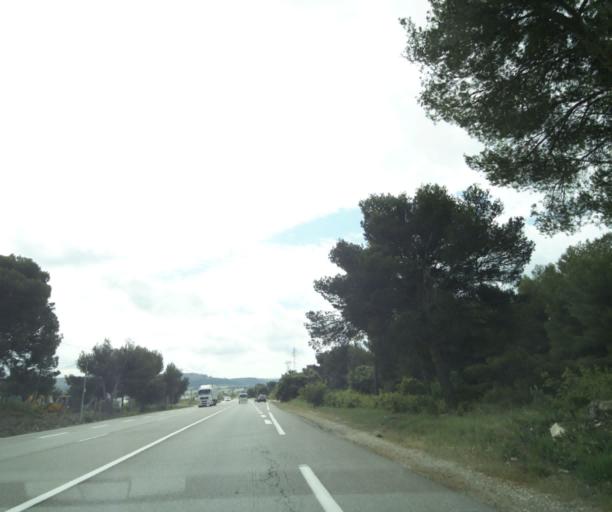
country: FR
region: Provence-Alpes-Cote d'Azur
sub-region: Departement des Bouches-du-Rhone
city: Rognac
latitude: 43.5043
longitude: 5.2095
